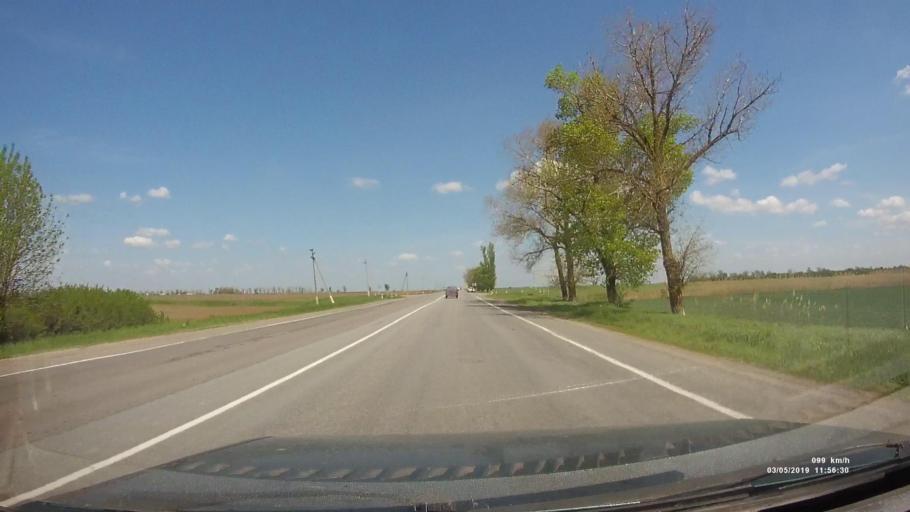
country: RU
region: Rostov
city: Bagayevskaya
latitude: 47.1955
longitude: 40.3016
